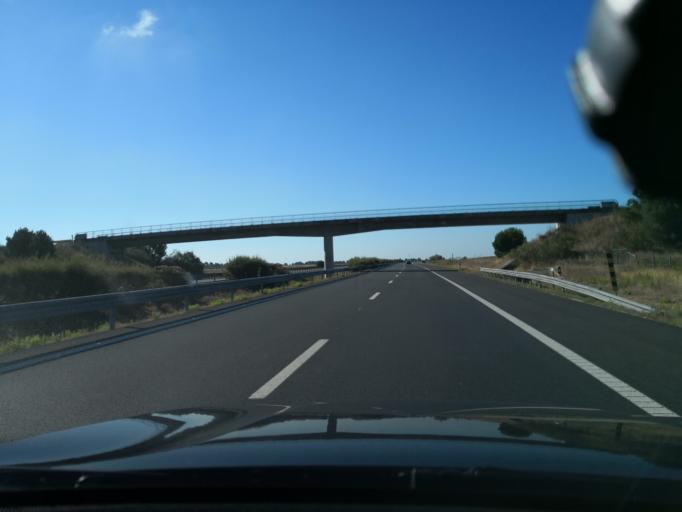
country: PT
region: Beja
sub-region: Aljustrel
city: Aljustrel
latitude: 37.9888
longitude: -8.2657
